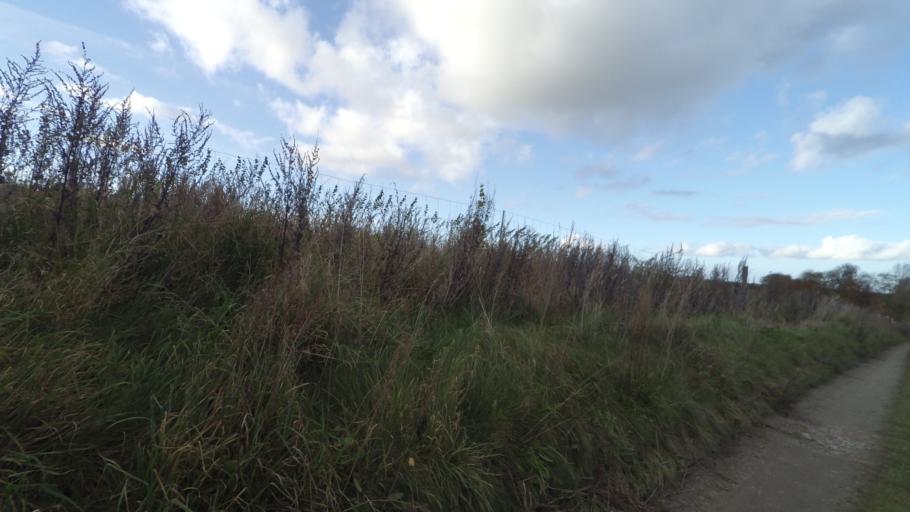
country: DK
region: Central Jutland
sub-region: Arhus Kommune
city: Kolt
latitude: 56.1287
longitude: 10.0760
